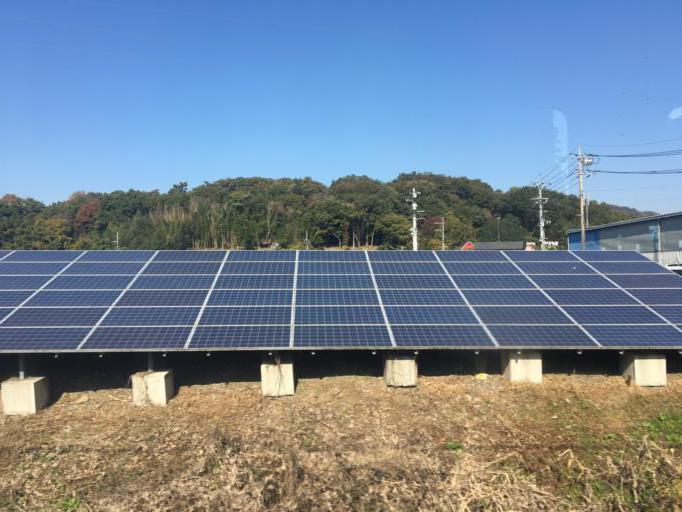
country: JP
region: Tochigi
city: Sano
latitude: 36.3231
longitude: 139.6188
